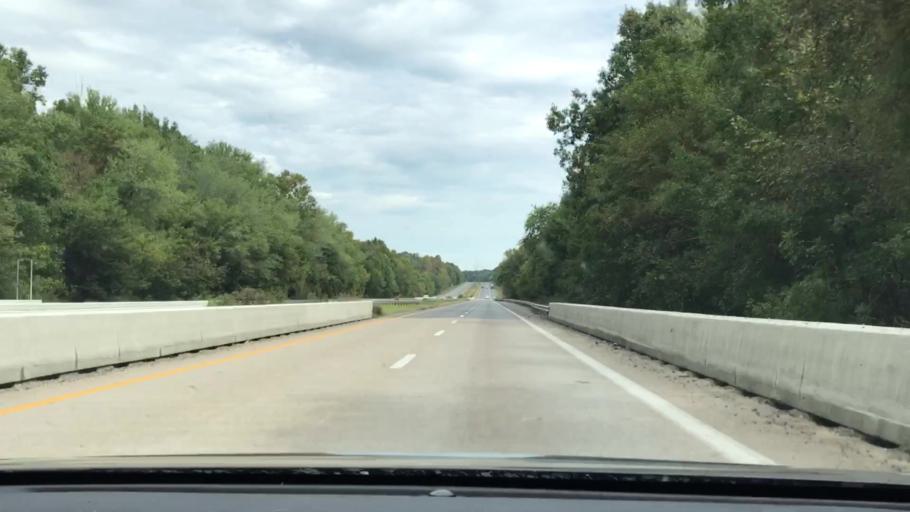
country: US
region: Kentucky
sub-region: Marshall County
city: Benton
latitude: 36.8836
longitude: -88.3559
